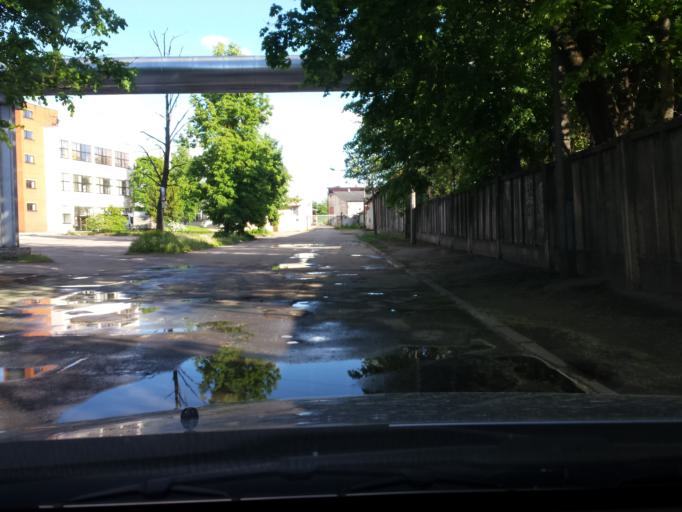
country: LV
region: Riga
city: Riga
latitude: 56.9802
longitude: 24.1527
